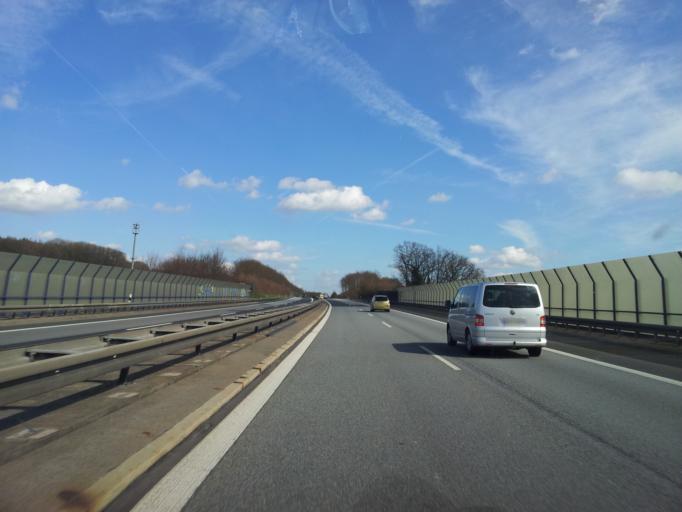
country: DE
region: Bavaria
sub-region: Regierungsbezirk Unterfranken
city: Gadheim
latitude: 50.0079
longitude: 10.3631
